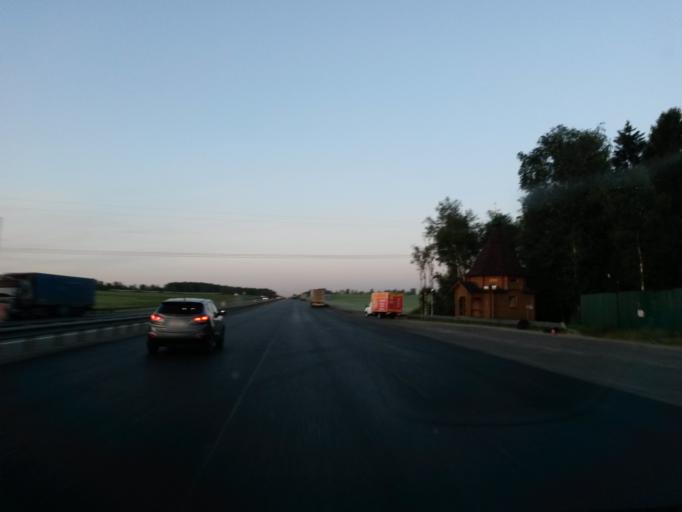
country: RU
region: Moskovskaya
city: Svatkovo
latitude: 56.3275
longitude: 38.2541
